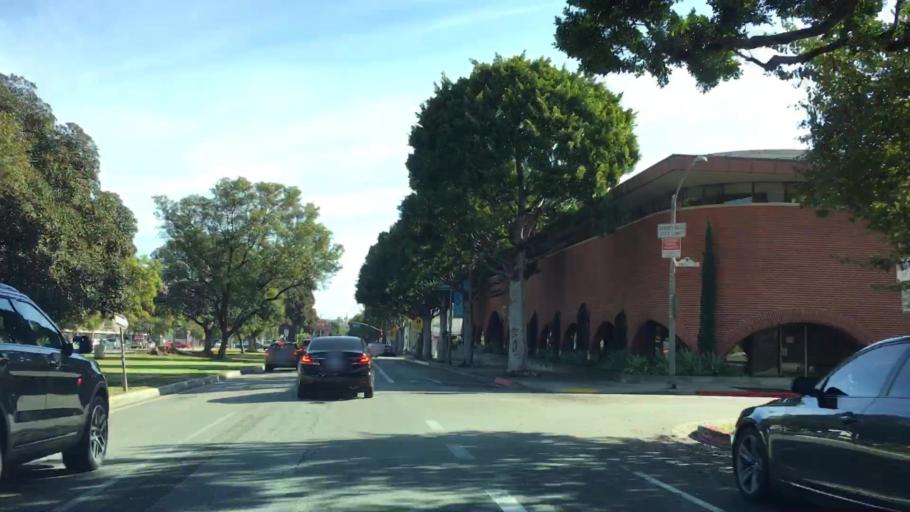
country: US
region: California
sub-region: Los Angeles County
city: Beverly Hills
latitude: 34.0721
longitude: -118.3868
